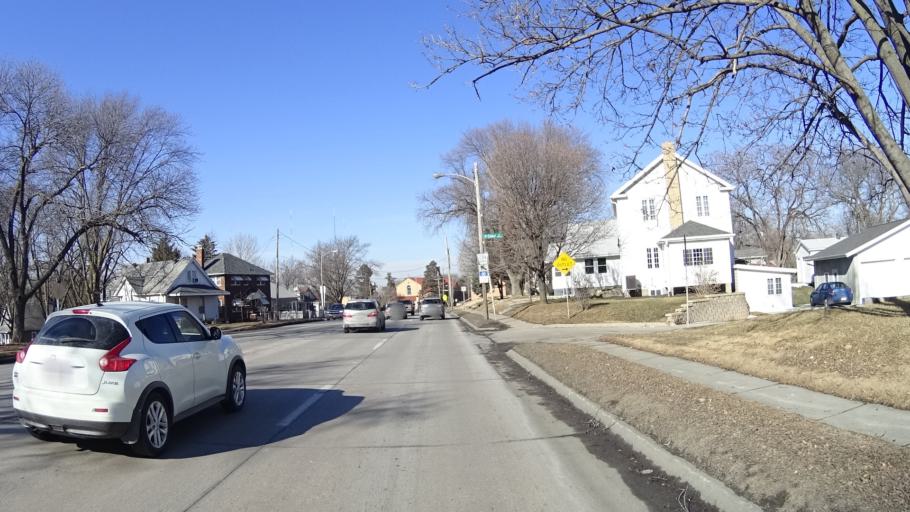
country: US
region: Nebraska
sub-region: Douglas County
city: Omaha
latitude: 41.2893
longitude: -96.0105
